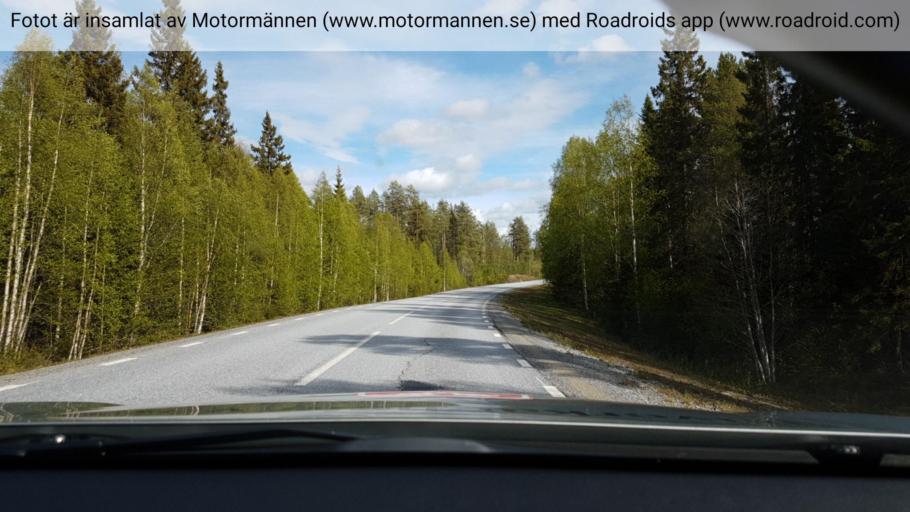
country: SE
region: Vaesterbotten
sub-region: Bjurholms Kommun
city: Bjurholm
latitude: 64.0235
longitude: 18.6651
